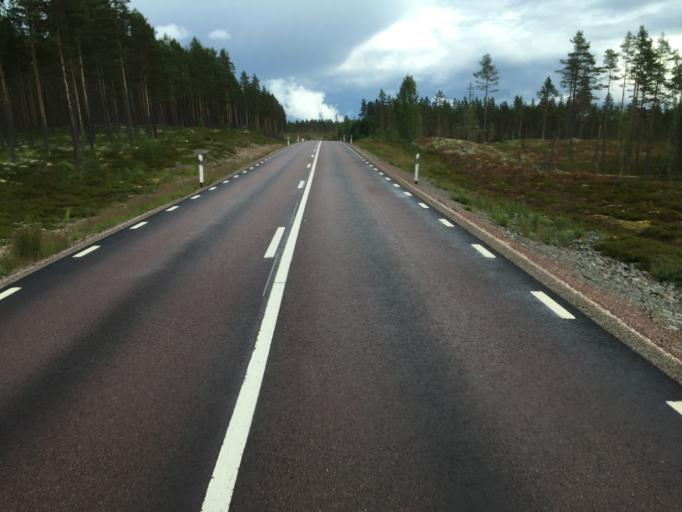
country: SE
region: Dalarna
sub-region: Malung-Saelens kommun
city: Malung
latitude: 60.8235
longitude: 13.9782
